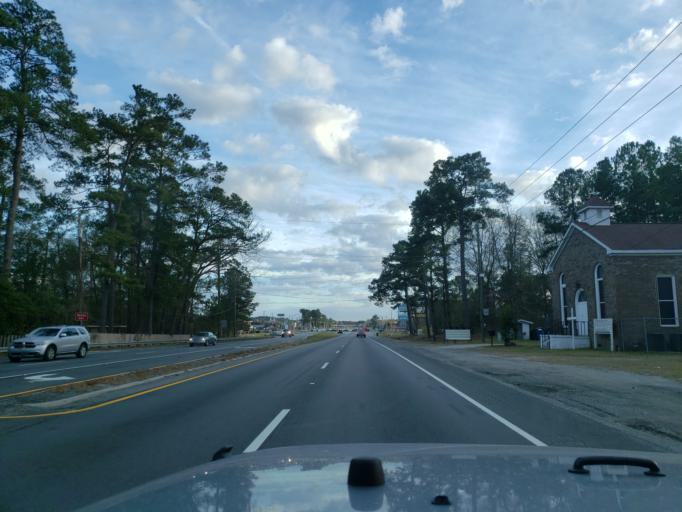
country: US
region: Georgia
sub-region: Chatham County
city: Port Wentworth
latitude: 32.2016
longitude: -81.1988
